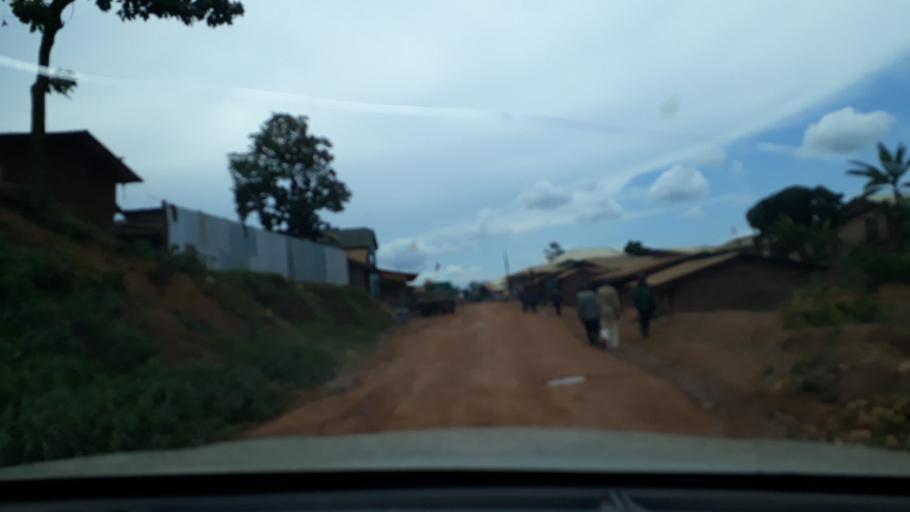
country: CD
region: Eastern Province
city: Bunia
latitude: 1.7371
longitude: 30.3392
